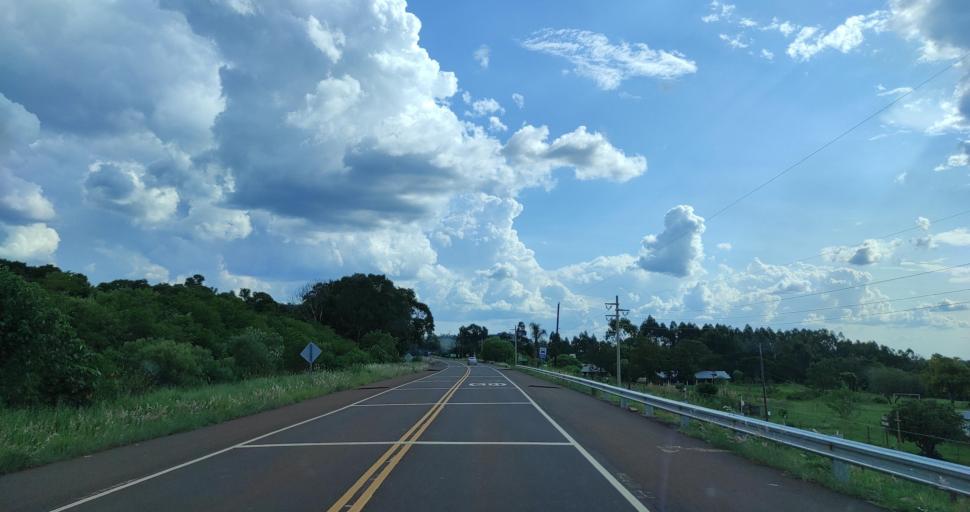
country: AR
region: Misiones
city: Bernardo de Irigoyen
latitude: -26.3090
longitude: -53.8220
